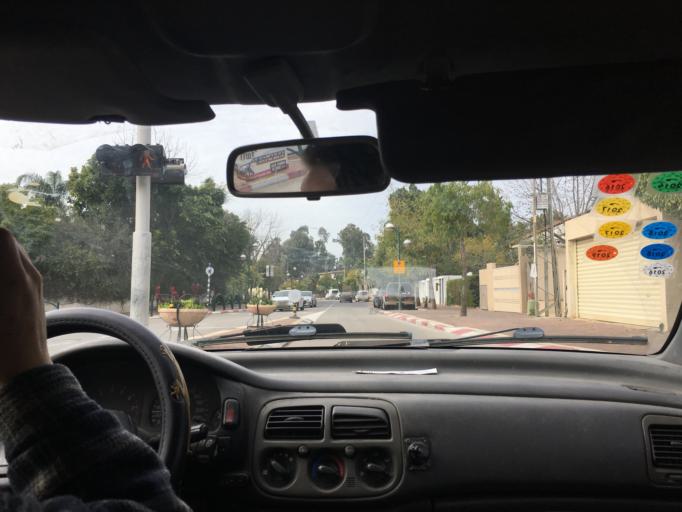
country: IL
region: Tel Aviv
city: Ramat HaSharon
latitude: 32.1358
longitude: 34.8498
